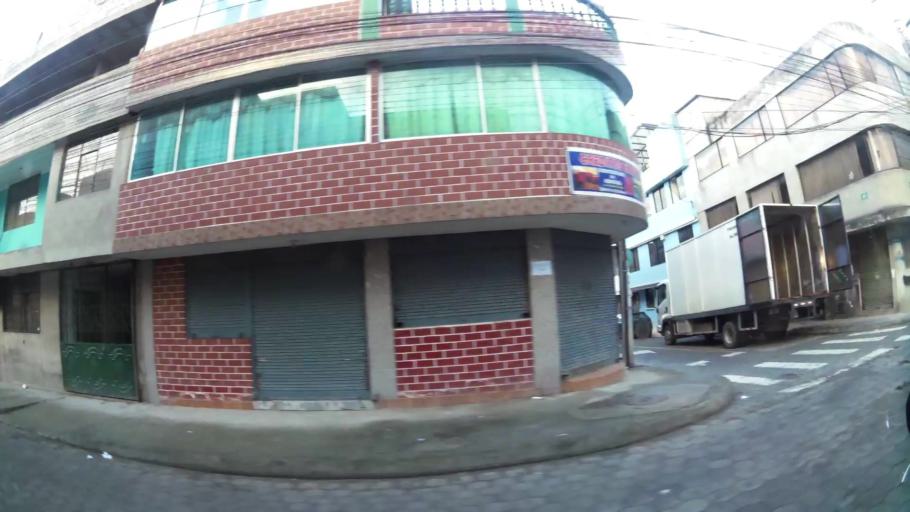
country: EC
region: Pichincha
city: Quito
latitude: -0.3064
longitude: -78.5414
